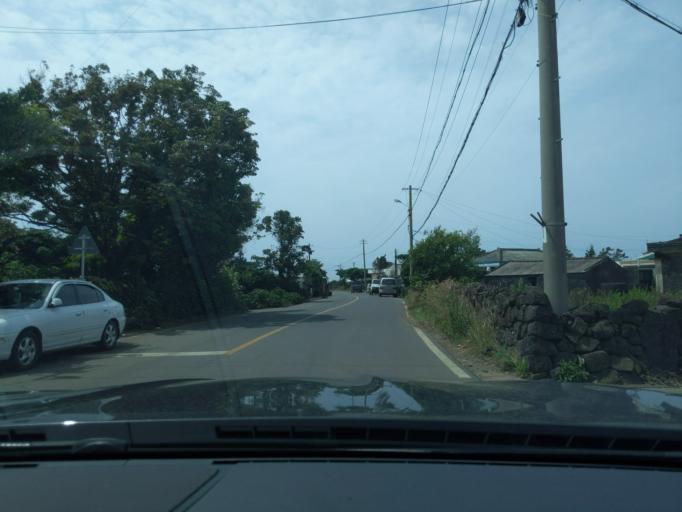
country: KR
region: Jeju-do
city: Gaigeturi
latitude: 33.2238
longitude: 126.2661
